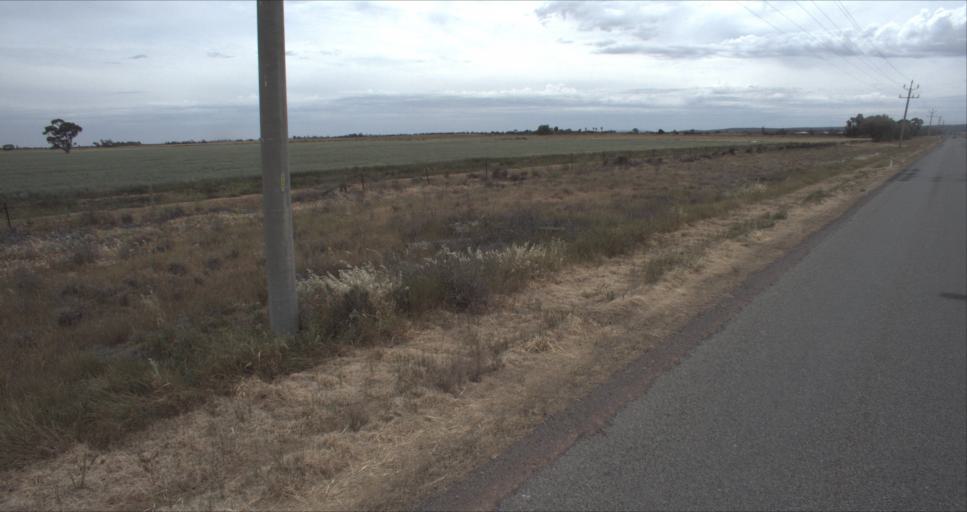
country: AU
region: New South Wales
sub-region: Leeton
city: Leeton
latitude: -34.4992
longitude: 146.4000
